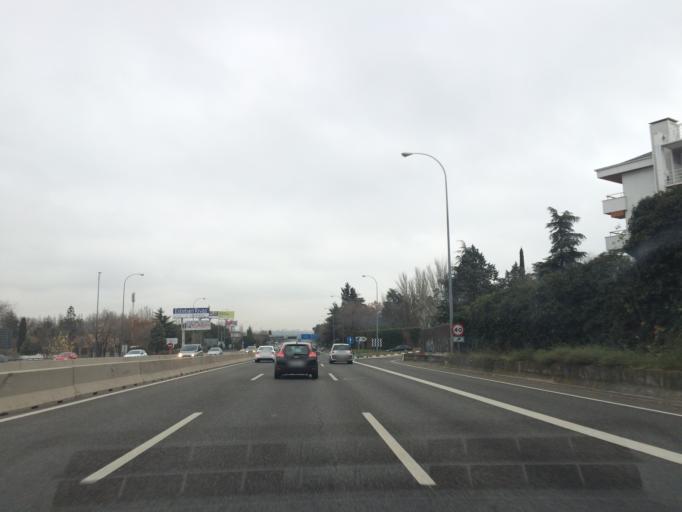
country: ES
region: Madrid
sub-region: Provincia de Madrid
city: Pozuelo de Alarcon
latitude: 40.4635
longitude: -3.7855
